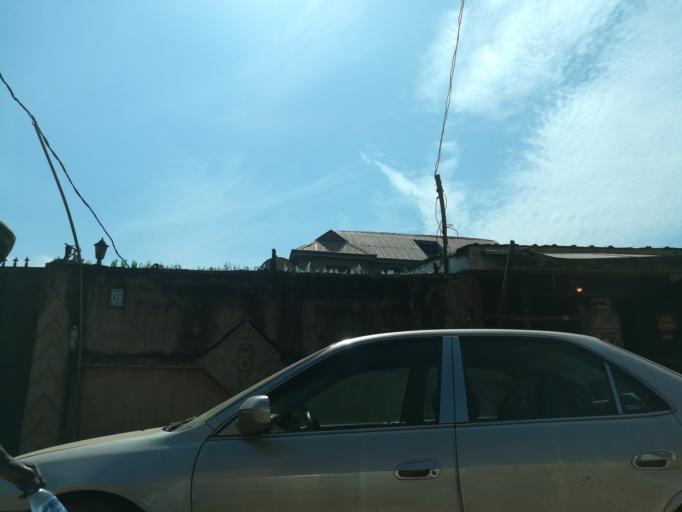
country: NG
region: Lagos
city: Ebute Ikorodu
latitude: 6.6266
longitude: 3.4831
